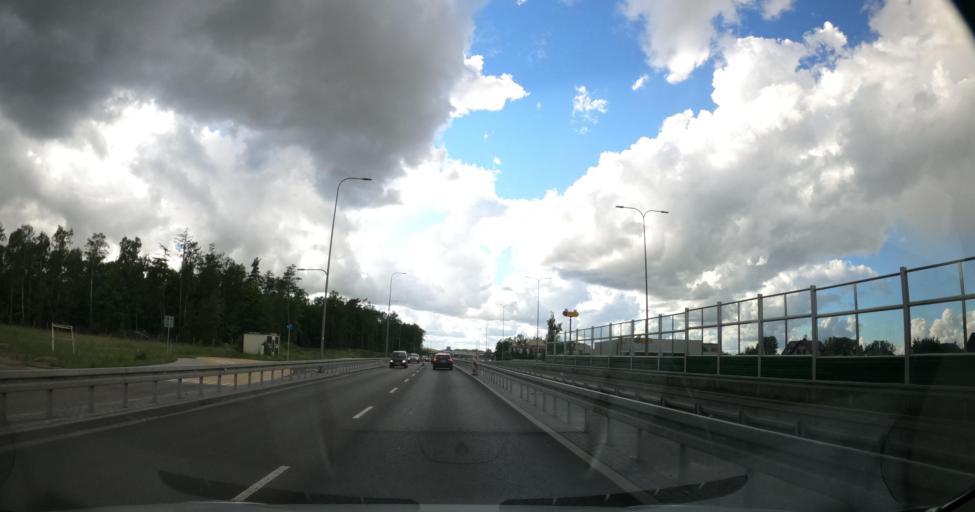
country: PL
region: Pomeranian Voivodeship
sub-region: Powiat gdanski
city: Lublewo Gdanskie
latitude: 54.3526
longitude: 18.4982
